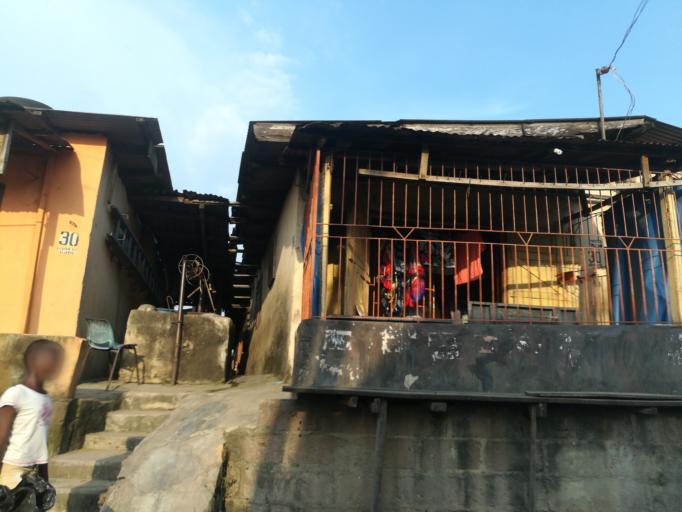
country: NG
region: Lagos
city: Ojota
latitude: 6.5899
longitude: 3.3964
